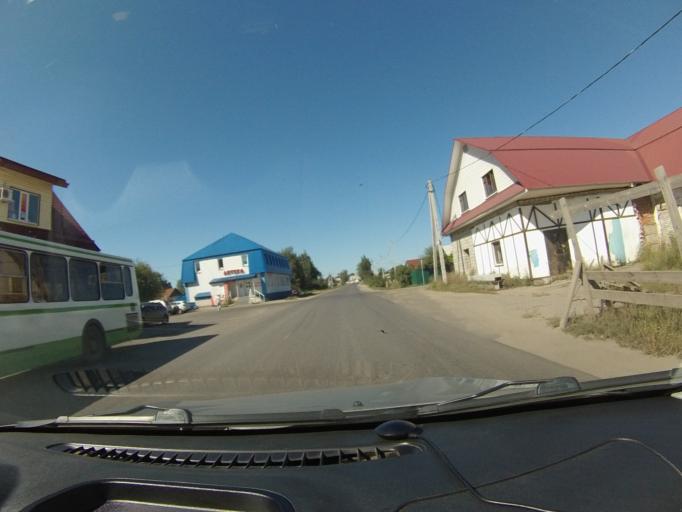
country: RU
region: Tambov
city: Donskoye
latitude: 52.7625
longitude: 41.4720
